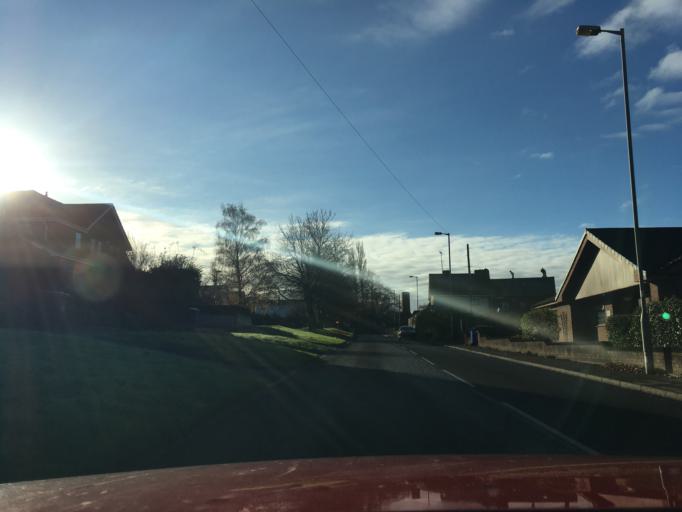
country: GB
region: England
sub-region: Staffordshire
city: Burton upon Trent
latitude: 52.8146
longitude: -1.6103
